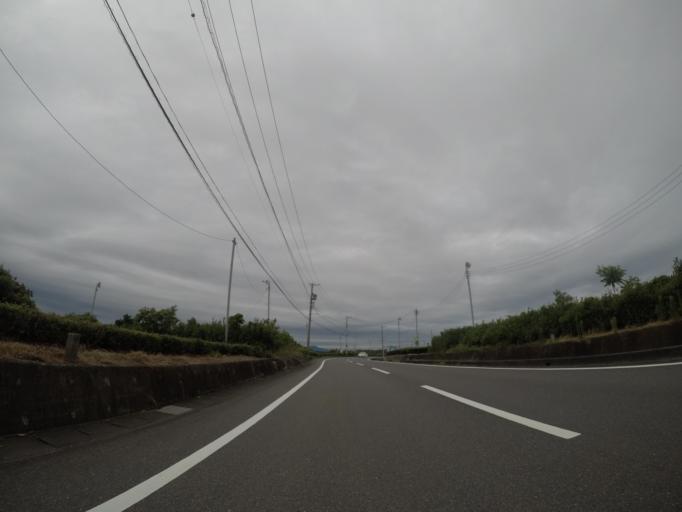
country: JP
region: Shizuoka
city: Sagara
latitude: 34.7358
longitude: 138.2025
